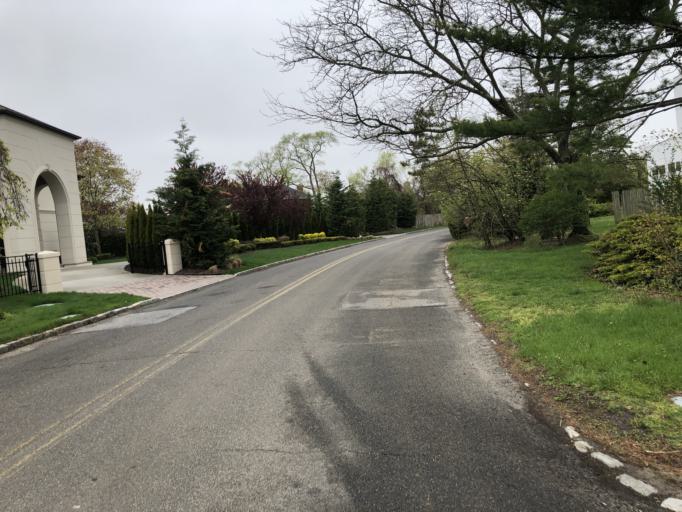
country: US
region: New York
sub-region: Nassau County
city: Hewlett Harbor
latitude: 40.6268
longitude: -73.6860
